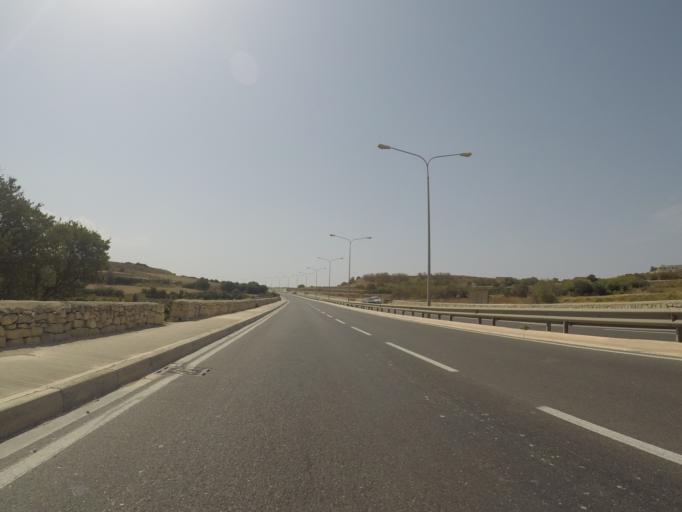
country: MT
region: L-Imdina
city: Imdina
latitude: 35.8874
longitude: 14.4105
